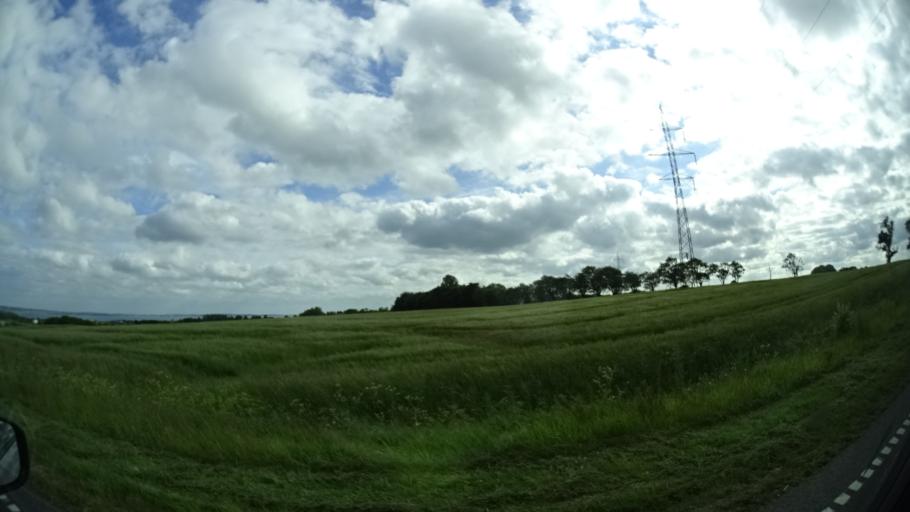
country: DK
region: Central Jutland
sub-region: Syddjurs Kommune
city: Ronde
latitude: 56.3183
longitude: 10.4196
